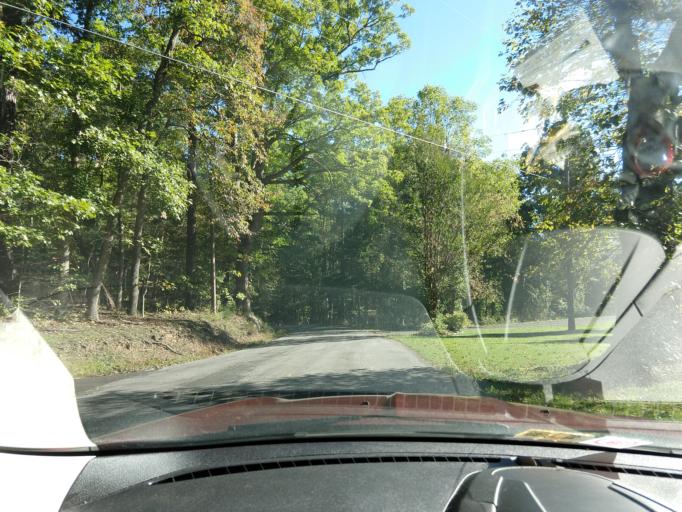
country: US
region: Virginia
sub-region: Alleghany County
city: Clifton Forge
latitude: 37.8493
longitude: -79.8466
